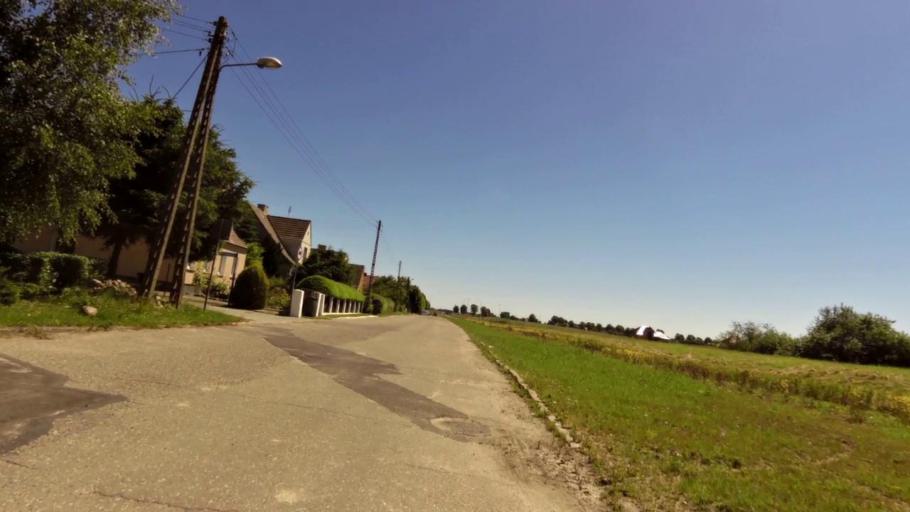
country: PL
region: West Pomeranian Voivodeship
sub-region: Powiat kolobrzeski
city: Goscino
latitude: 54.0521
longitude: 15.6461
